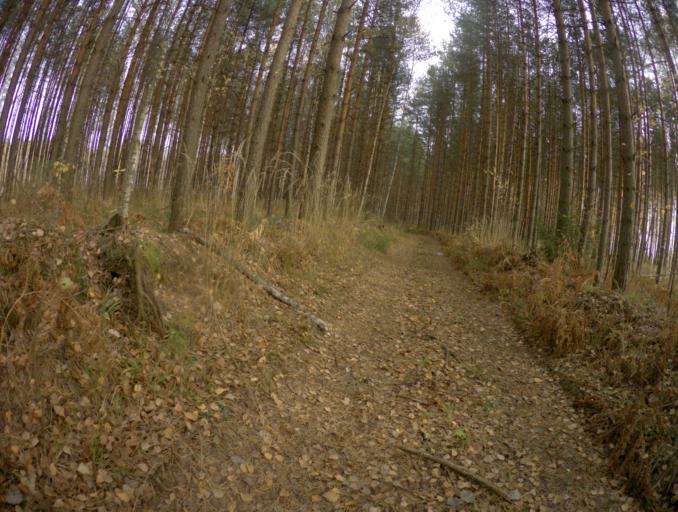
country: RU
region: Vladimir
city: Sobinka
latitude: 55.9758
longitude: 40.0741
